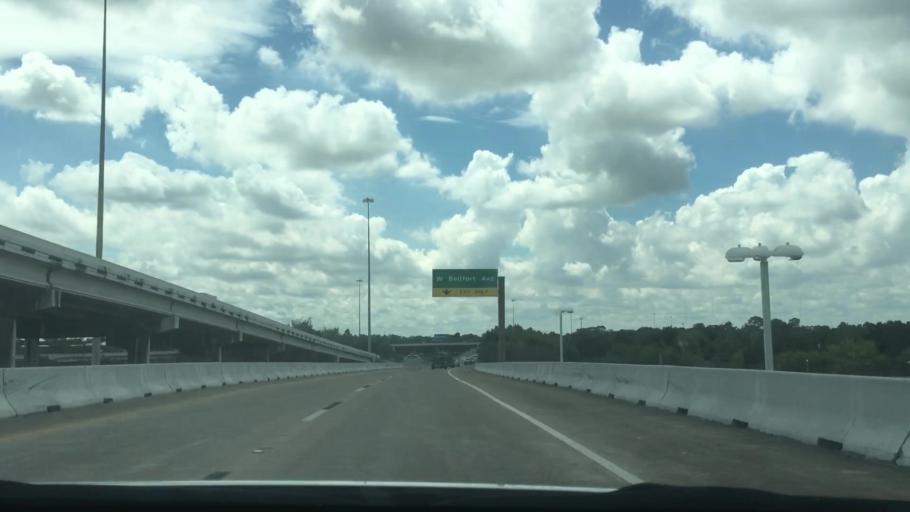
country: US
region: Texas
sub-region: Harris County
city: Bellaire
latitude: 29.6808
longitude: -95.4591
